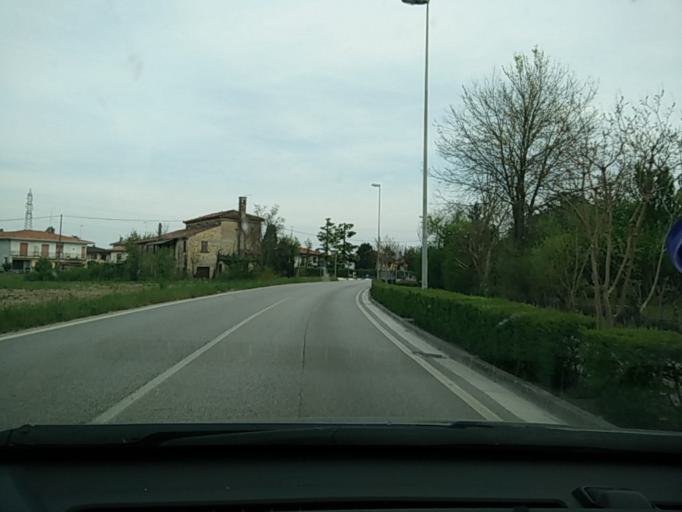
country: IT
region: Veneto
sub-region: Provincia di Treviso
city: Salgareda
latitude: 45.7122
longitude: 12.4820
